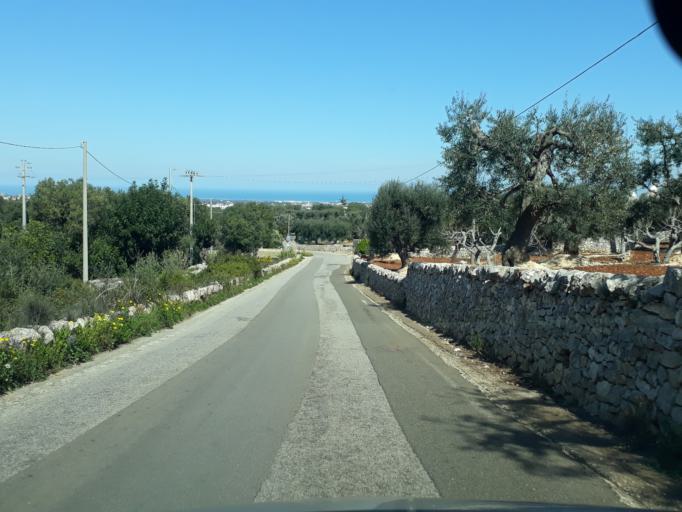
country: IT
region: Apulia
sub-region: Provincia di Brindisi
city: Lamie di Olimpie-Selva
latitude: 40.8124
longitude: 17.3559
